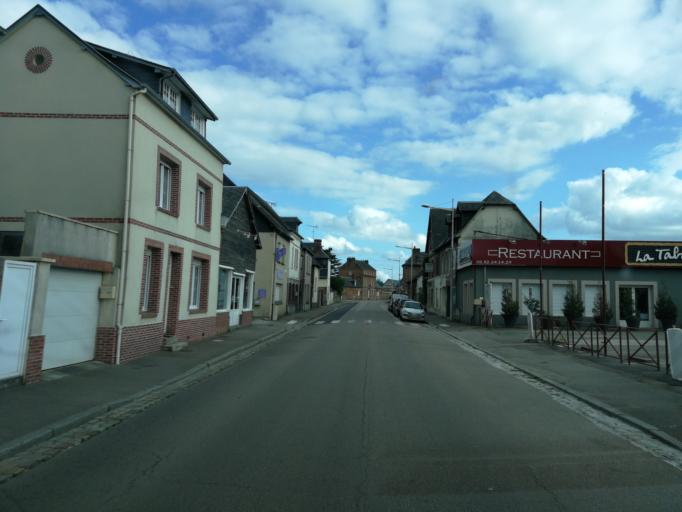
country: FR
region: Haute-Normandie
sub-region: Departement de l'Eure
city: Le Neubourg
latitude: 49.1461
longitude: 0.9019
